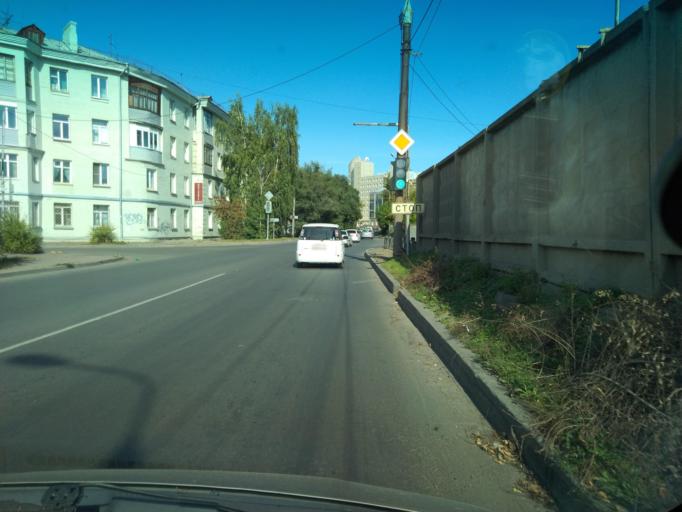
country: RU
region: Krasnoyarskiy
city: Krasnoyarsk
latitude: 56.0098
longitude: 92.9720
